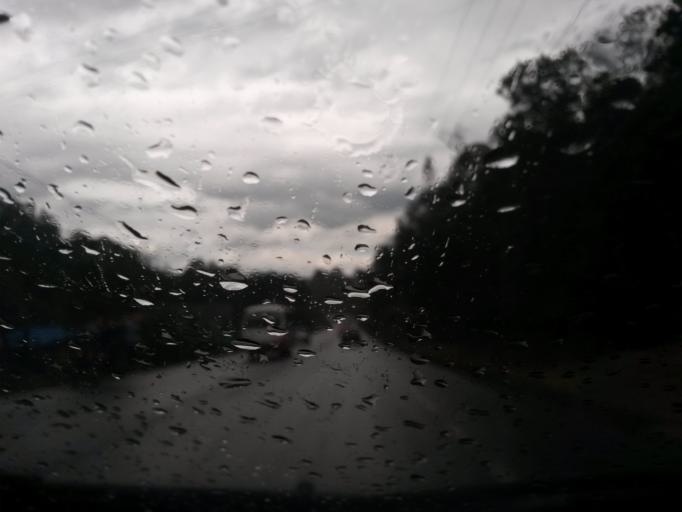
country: CO
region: Cauca
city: Popayan
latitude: 2.5047
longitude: -76.5522
